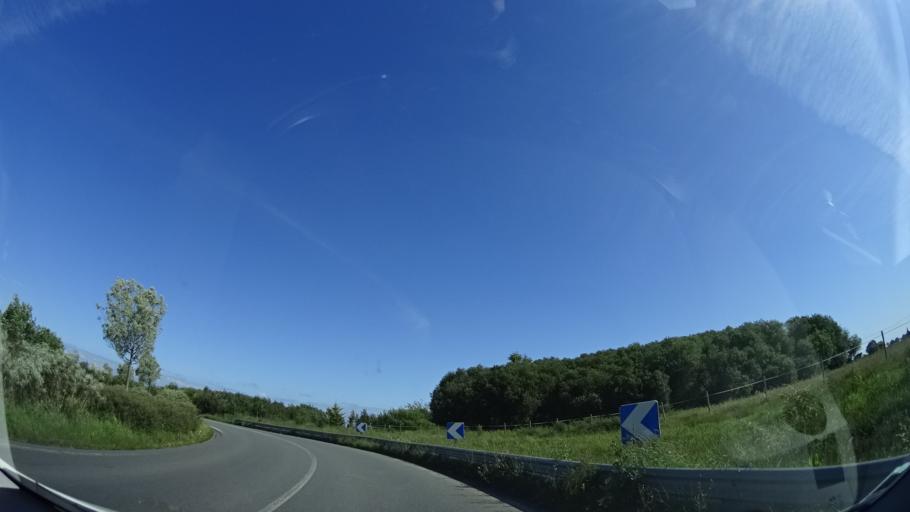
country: FR
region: Brittany
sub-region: Departement d'Ille-et-Vilaine
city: Saint-Jouan-des-Guerets
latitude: 48.6112
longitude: -1.9703
